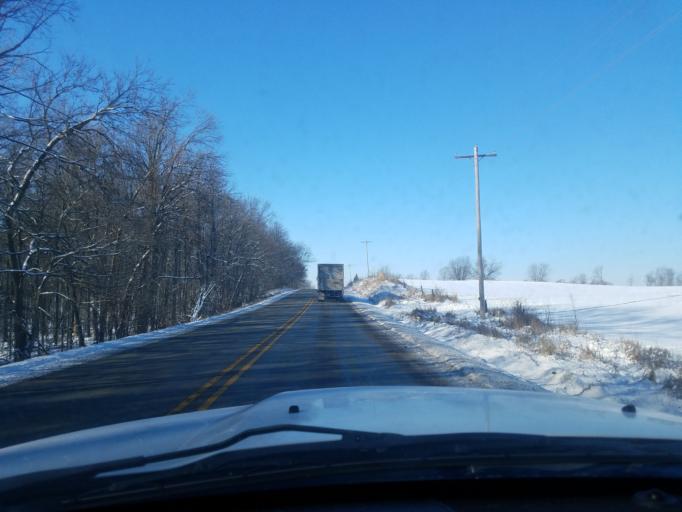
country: US
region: Indiana
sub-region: Noble County
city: Kendallville
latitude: 41.3951
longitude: -85.3158
